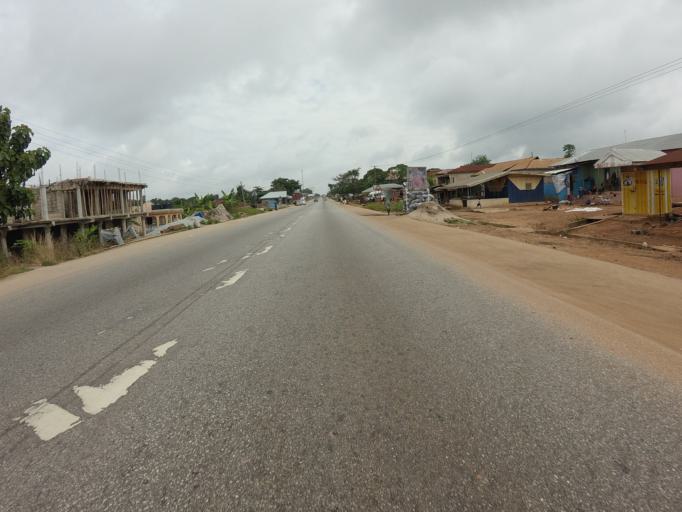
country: GH
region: Ashanti
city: Tafo
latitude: 6.9652
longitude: -1.6799
